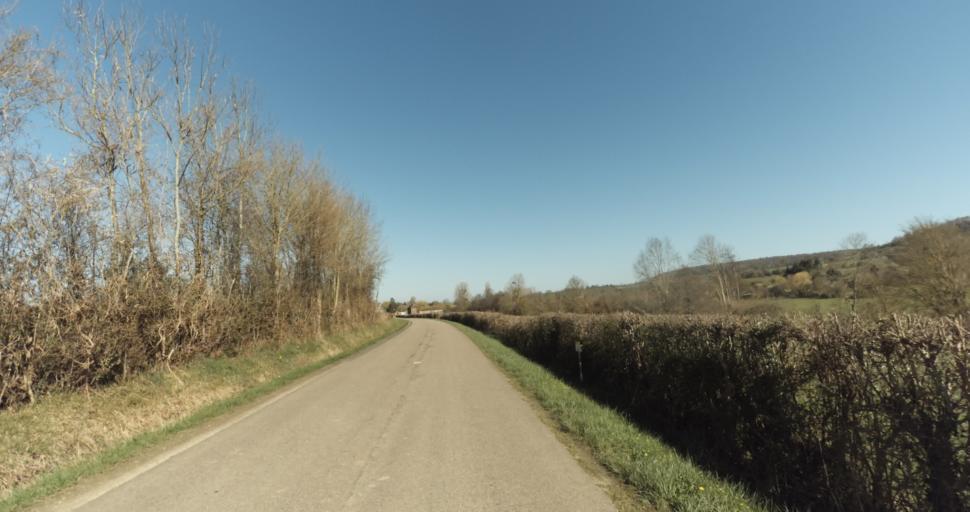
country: FR
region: Lower Normandy
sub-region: Departement du Calvados
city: Saint-Pierre-sur-Dives
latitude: 48.9836
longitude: 0.0327
